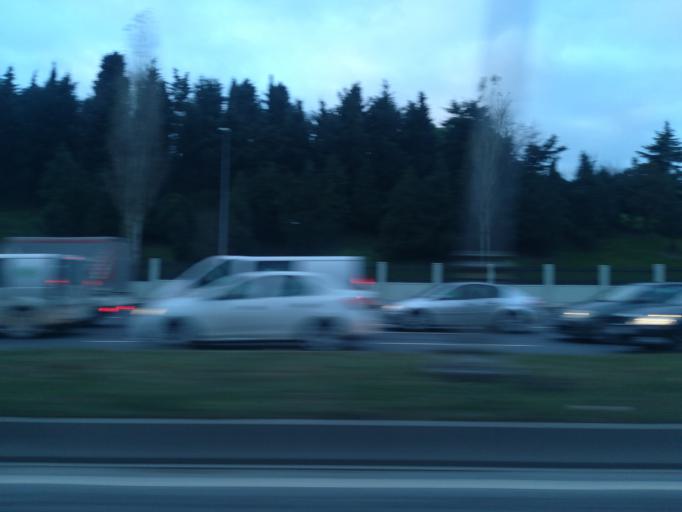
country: TR
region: Istanbul
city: Istanbul
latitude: 41.0266
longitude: 28.9266
